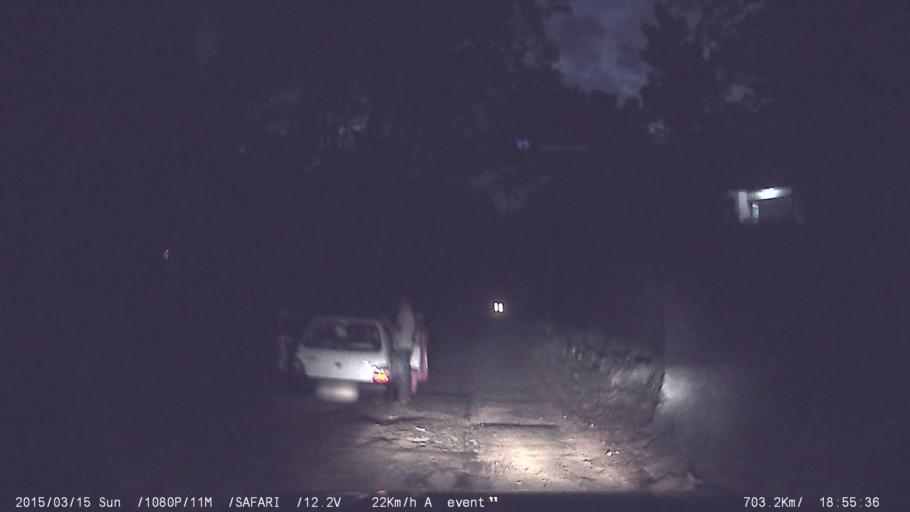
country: IN
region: Kerala
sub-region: Kottayam
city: Palackattumala
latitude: 9.8593
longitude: 76.6762
